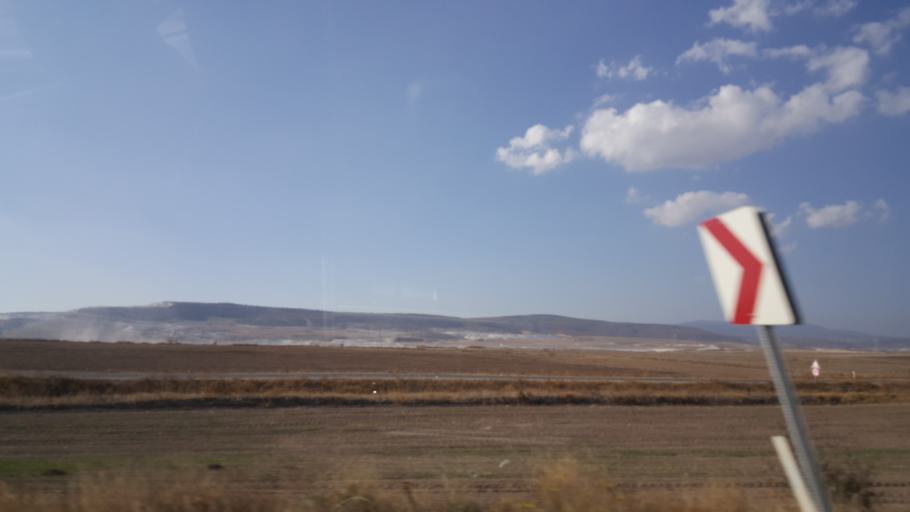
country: TR
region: Eskisehir
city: Kirka
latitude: 39.3034
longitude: 30.5297
